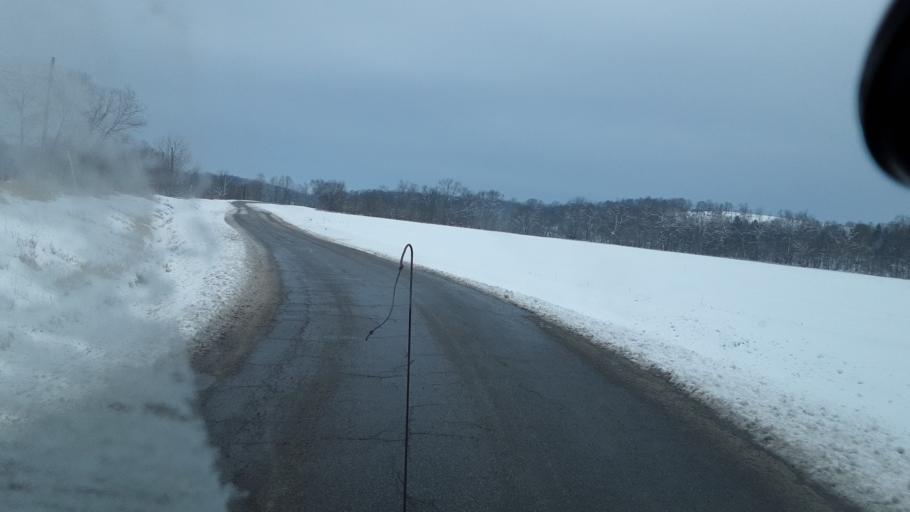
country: US
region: Ohio
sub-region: Perry County
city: Somerset
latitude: 39.8849
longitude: -82.2176
